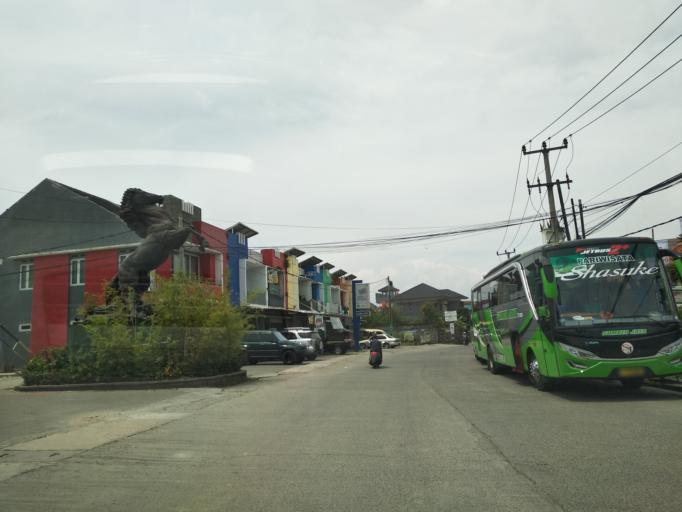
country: ID
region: West Java
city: Pameungpeuk
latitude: -6.9714
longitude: 107.6453
